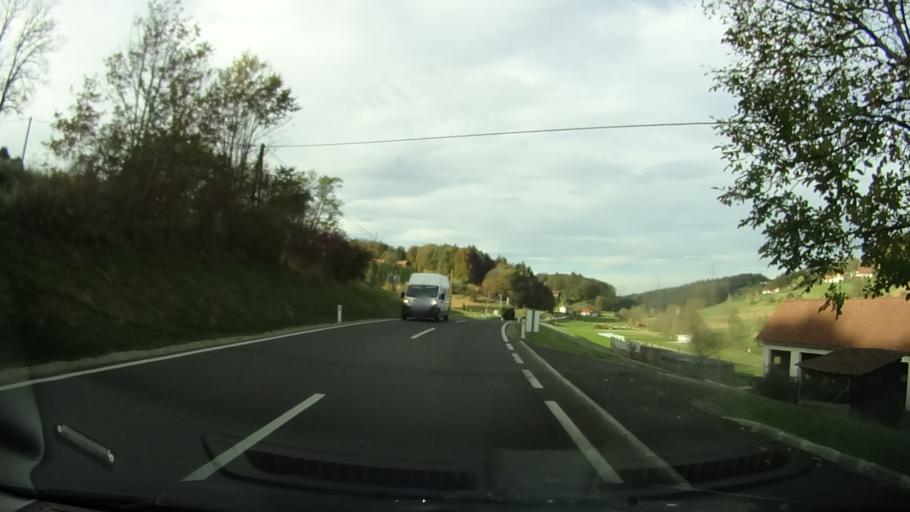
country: AT
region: Styria
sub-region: Politischer Bezirk Deutschlandsberg
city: Preding
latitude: 46.8720
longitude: 15.4080
